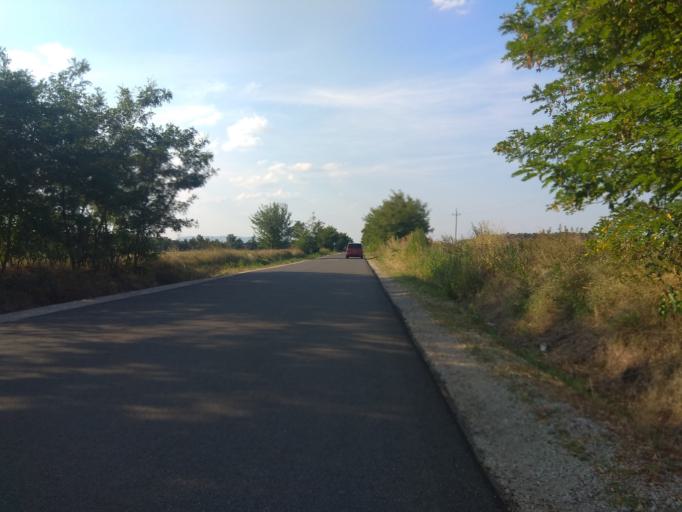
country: HU
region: Borsod-Abauj-Zemplen
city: Harsany
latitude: 47.8994
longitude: 20.7454
